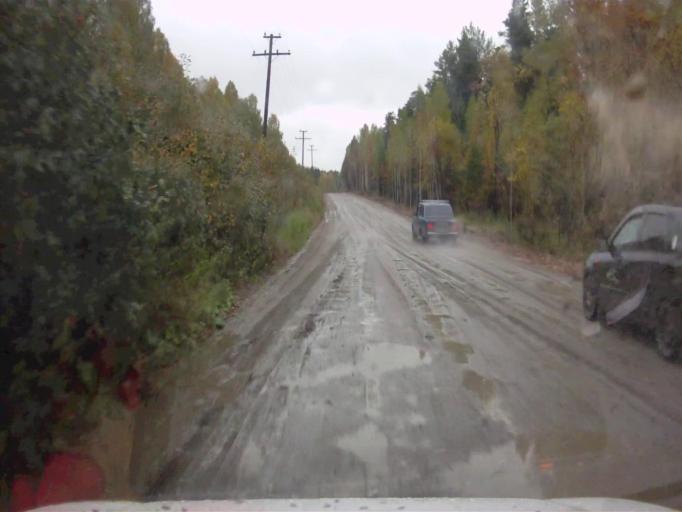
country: RU
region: Chelyabinsk
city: Kyshtym
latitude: 55.7969
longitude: 60.4815
